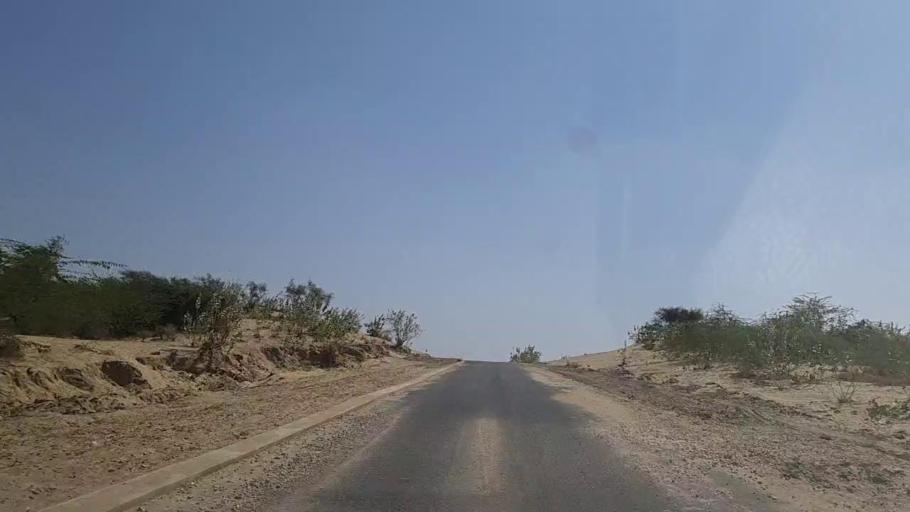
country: PK
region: Sindh
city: Diplo
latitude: 24.4846
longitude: 69.4682
